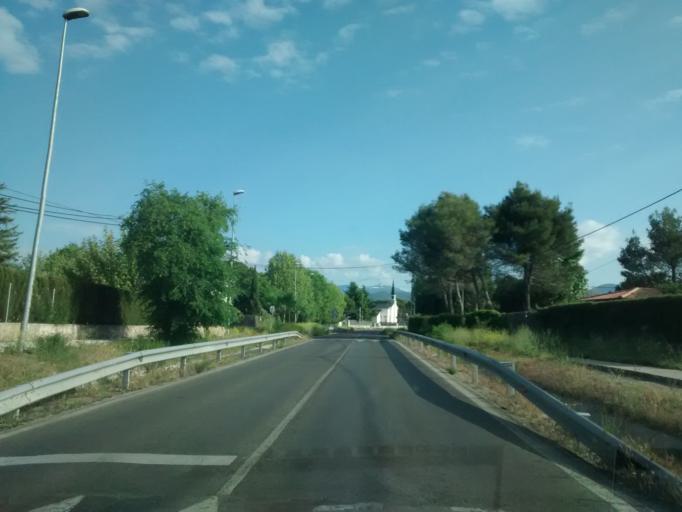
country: ES
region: Madrid
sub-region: Provincia de Madrid
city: Alpedrete
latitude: 40.6420
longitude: -4.0215
